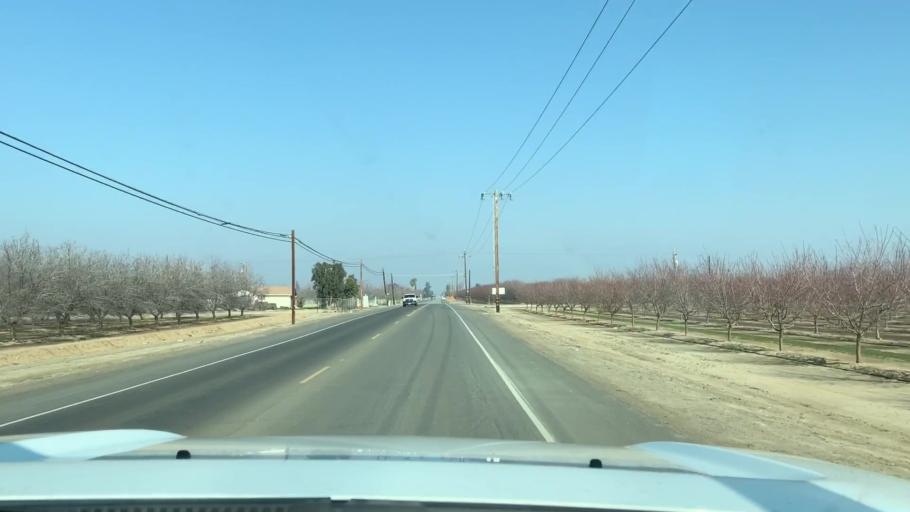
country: US
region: California
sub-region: Kern County
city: Shafter
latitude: 35.4840
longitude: -119.2785
